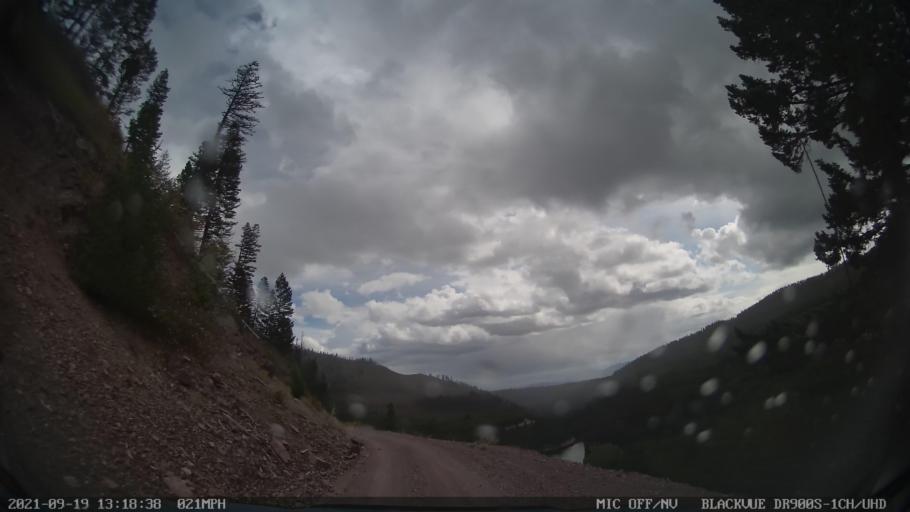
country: US
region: Montana
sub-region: Missoula County
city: Seeley Lake
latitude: 47.1707
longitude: -113.3555
